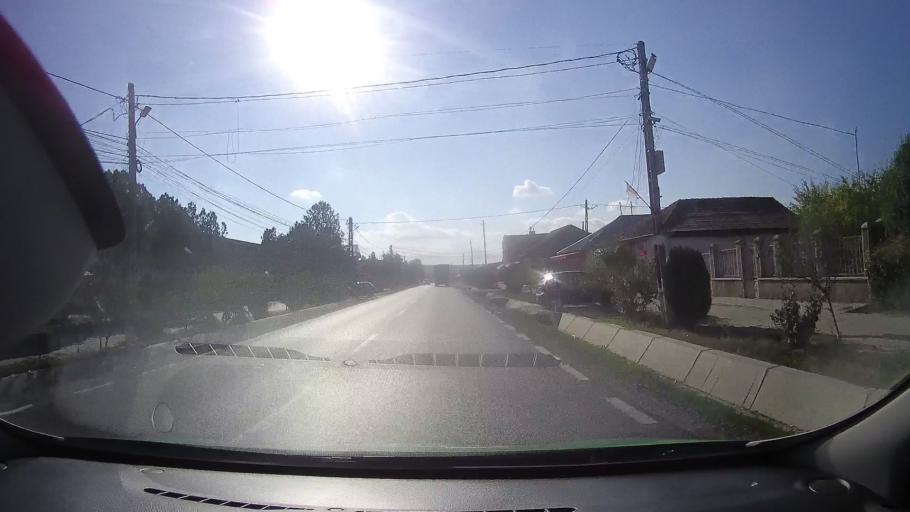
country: RO
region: Tulcea
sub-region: Comuna Baia
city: Baia
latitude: 44.7267
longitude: 28.6805
